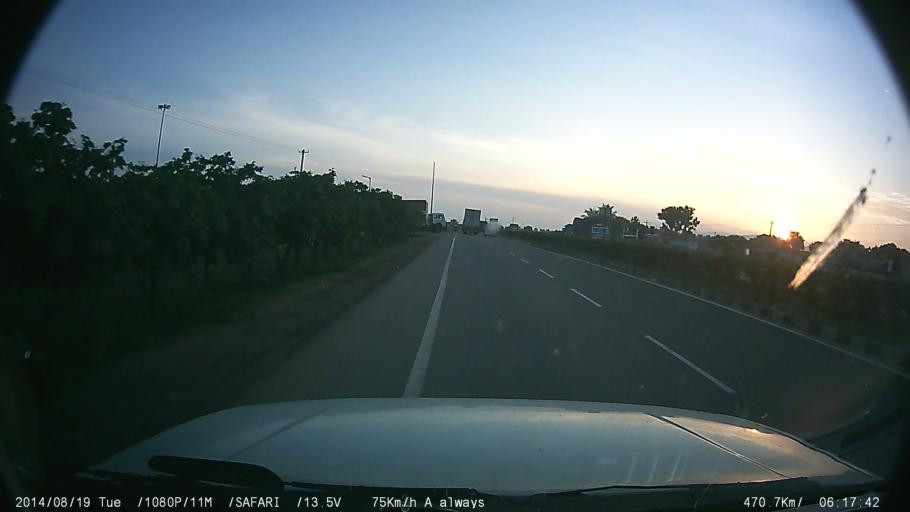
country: IN
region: Tamil Nadu
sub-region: Dharmapuri
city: Dharmapuri
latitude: 11.9977
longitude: 78.0723
